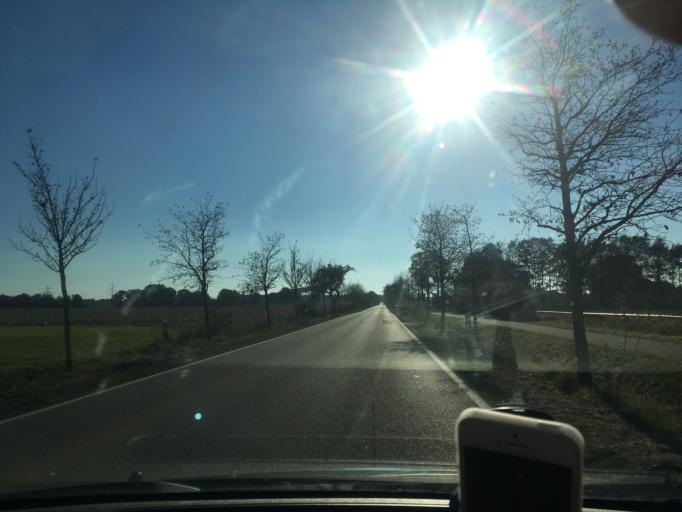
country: DE
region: Mecklenburg-Vorpommern
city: Wittenburg
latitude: 53.5261
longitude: 11.1048
